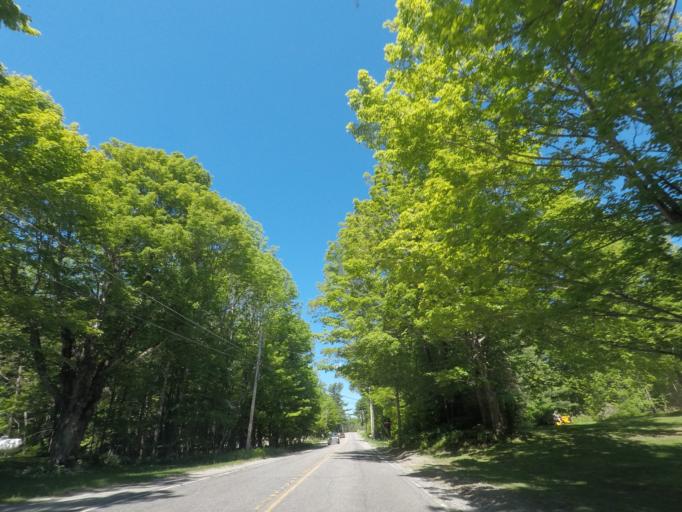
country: US
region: Maine
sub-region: Kennebec County
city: Gardiner
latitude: 44.2280
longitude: -69.8590
